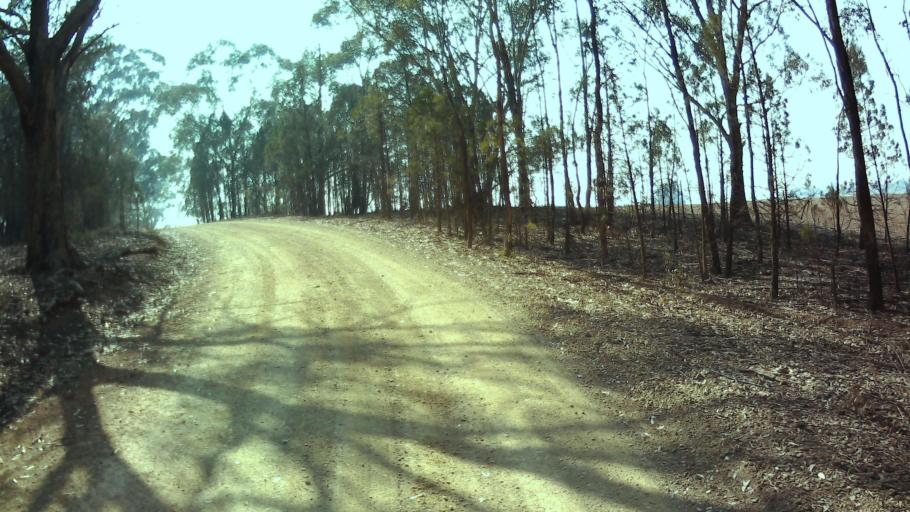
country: AU
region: New South Wales
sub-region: Weddin
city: Grenfell
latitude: -33.8957
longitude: 148.1787
